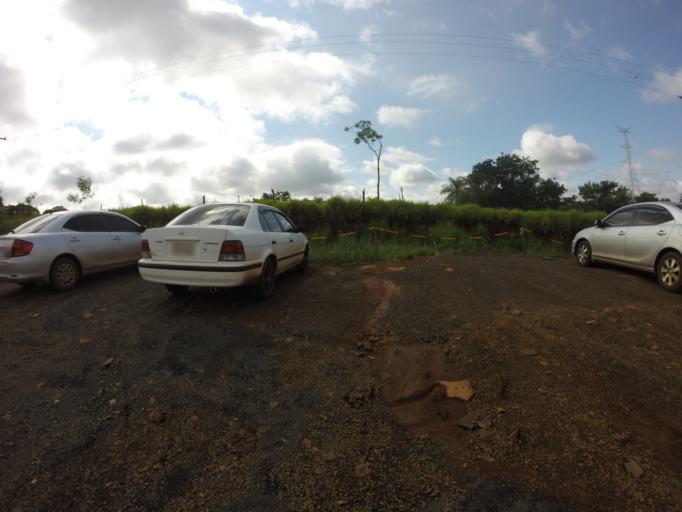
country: PY
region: Alto Parana
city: Ciudad del Este
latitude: -25.4103
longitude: -54.6659
